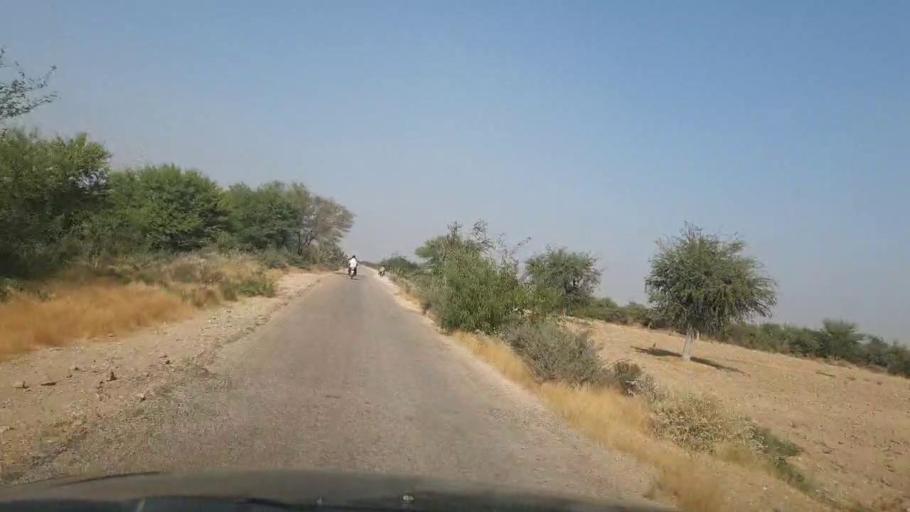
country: PK
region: Sindh
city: Jamshoro
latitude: 25.5305
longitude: 67.8230
